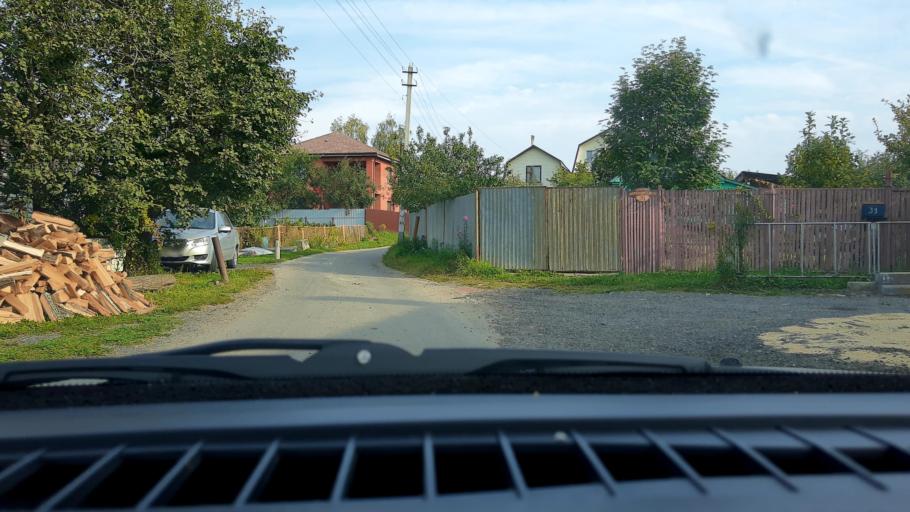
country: RU
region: Nizjnij Novgorod
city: Afonino
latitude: 56.1919
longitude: 44.0660
